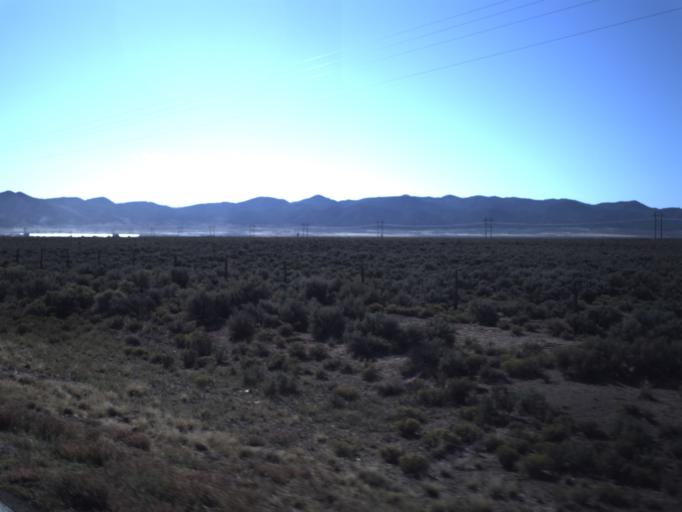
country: US
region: Utah
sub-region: Washington County
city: Enterprise
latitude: 37.6947
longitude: -113.6152
